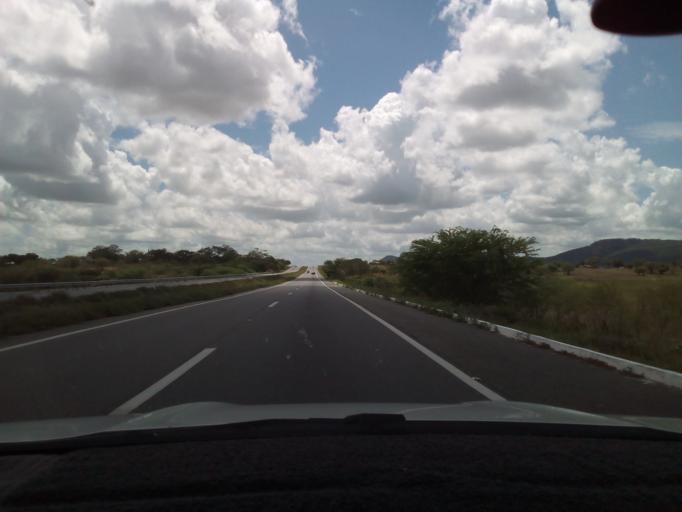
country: BR
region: Paraiba
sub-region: Gurinhem
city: Gurinhem
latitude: -7.1933
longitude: -35.4799
